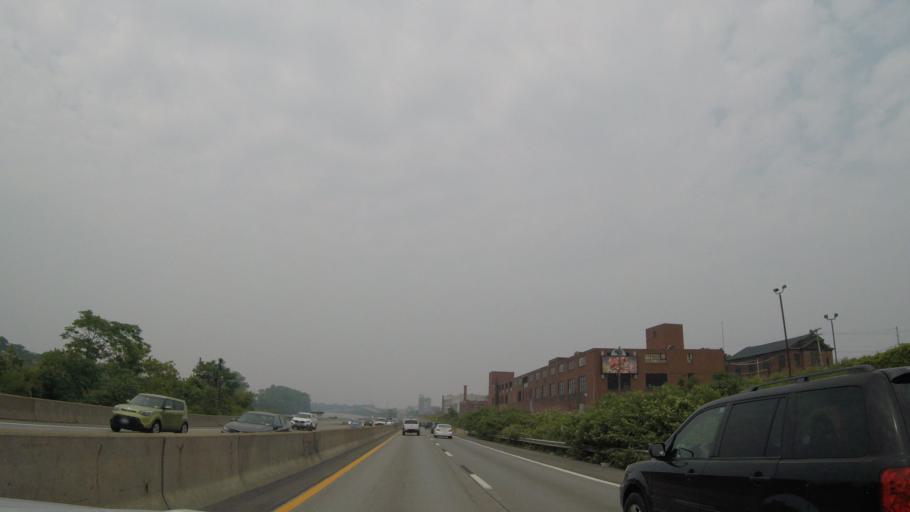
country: CA
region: Ontario
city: Fort Erie
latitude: 42.9168
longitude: -78.9011
